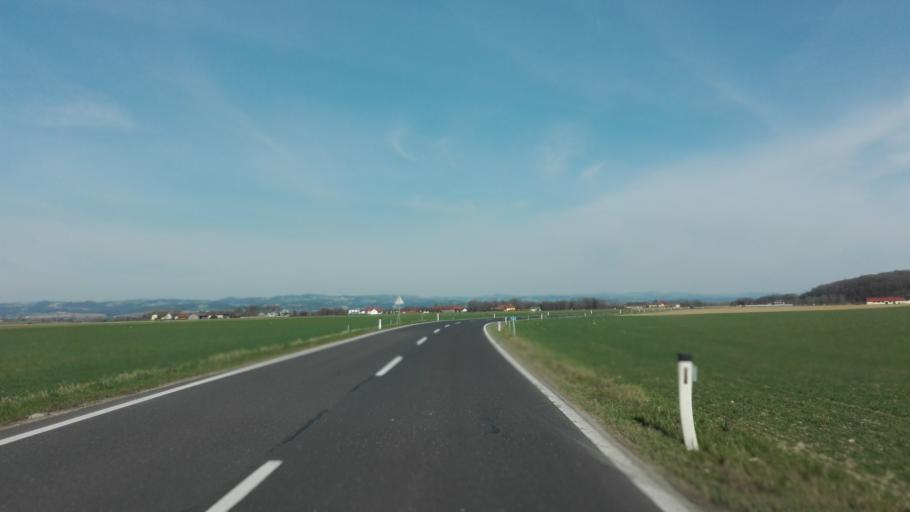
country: AT
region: Lower Austria
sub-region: Politischer Bezirk Amstetten
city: Ennsdorf
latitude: 48.2030
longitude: 14.5356
